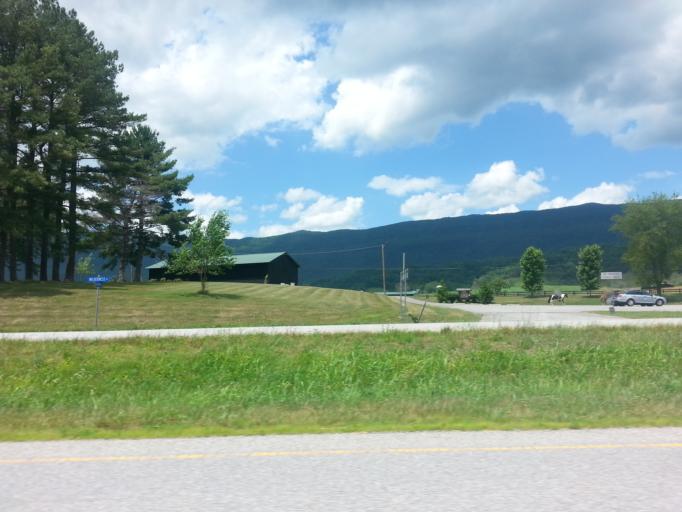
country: US
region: Tennessee
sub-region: Claiborne County
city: Harrogate
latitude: 36.6319
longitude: -83.4903
